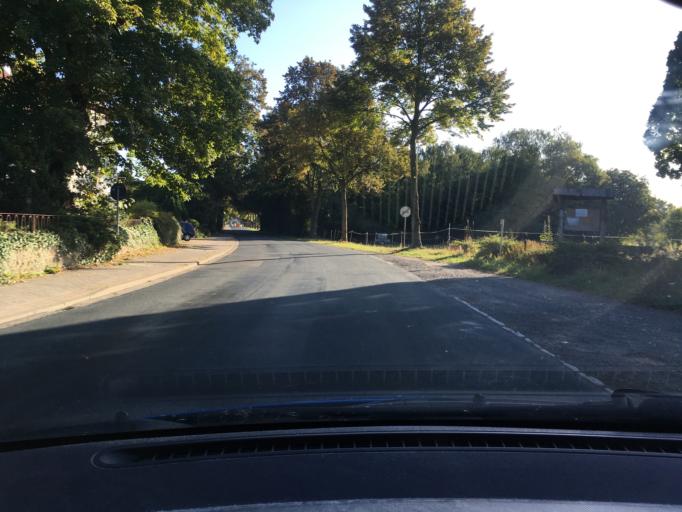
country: DE
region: Lower Saxony
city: Springe
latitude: 52.2022
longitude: 9.5366
